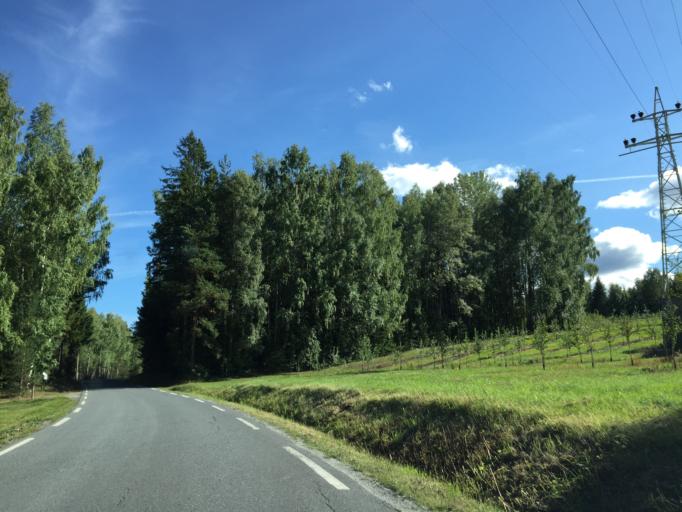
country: NO
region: Buskerud
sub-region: Ovre Eiker
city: Hokksund
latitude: 59.6943
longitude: 9.8417
